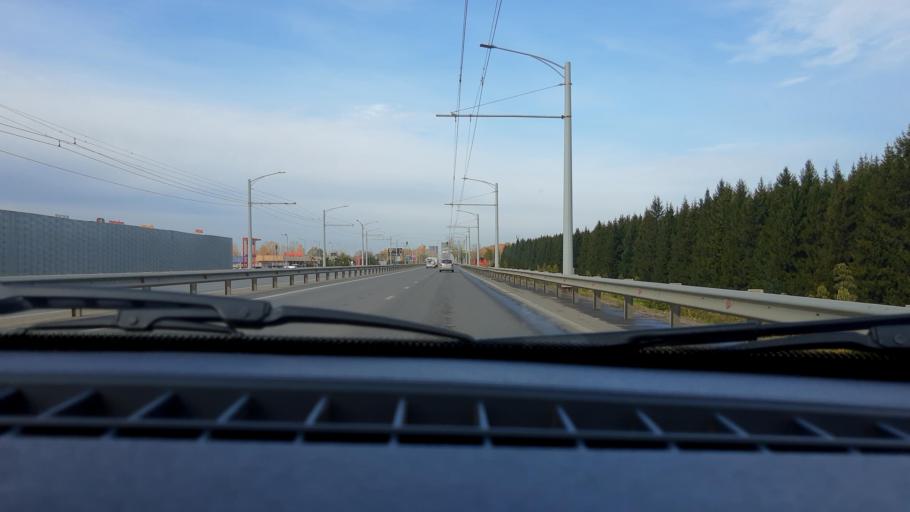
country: RU
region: Bashkortostan
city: Ufa
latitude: 54.7660
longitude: 55.9452
